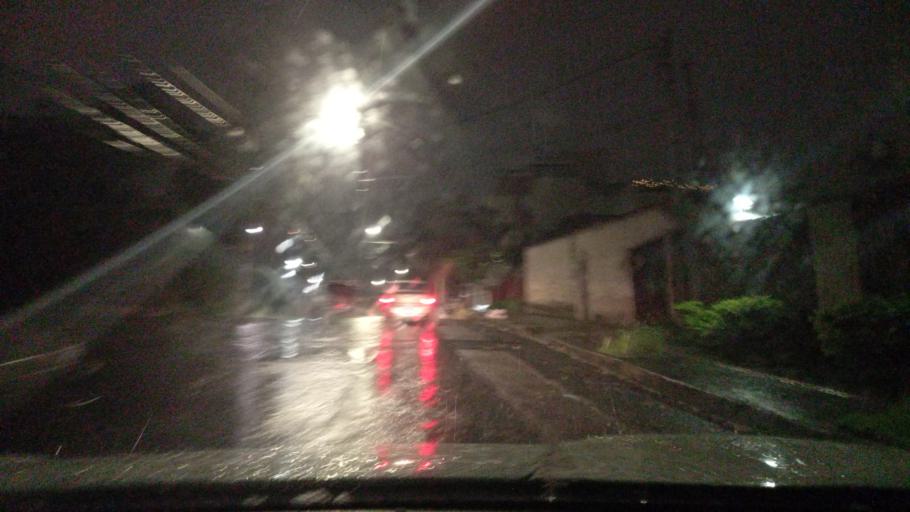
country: BR
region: Minas Gerais
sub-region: Belo Horizonte
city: Belo Horizonte
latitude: -19.9038
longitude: -43.9786
